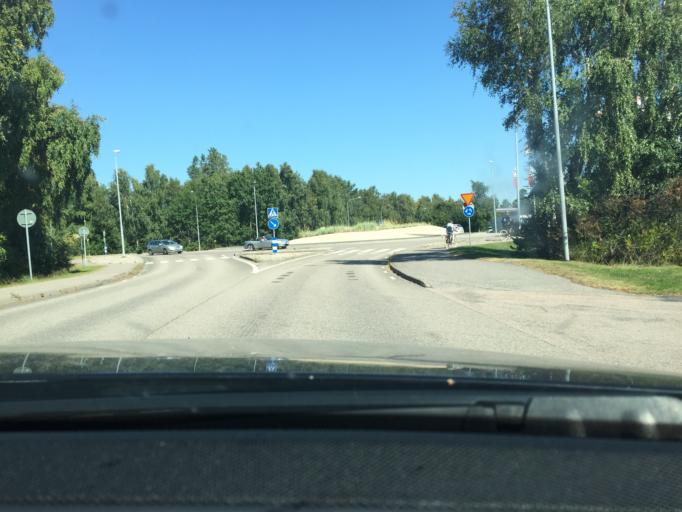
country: SE
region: Halland
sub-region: Laholms Kommun
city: Mellbystrand
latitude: 56.5039
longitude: 12.9552
